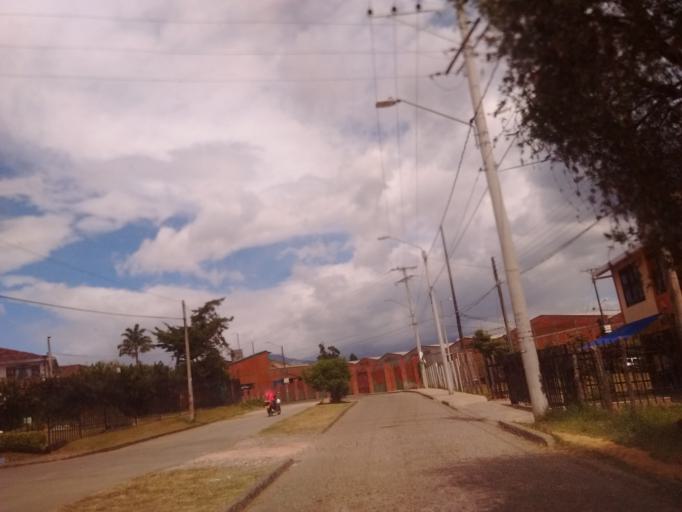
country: CO
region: Cauca
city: Popayan
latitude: 2.4905
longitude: -76.5622
